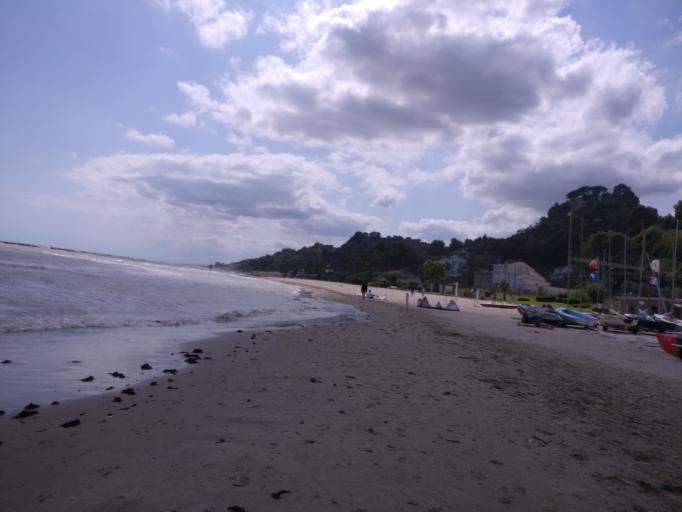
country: IT
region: The Marches
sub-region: Provincia di Ascoli Piceno
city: Cupra Marittima
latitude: 43.0210
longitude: 13.8623
